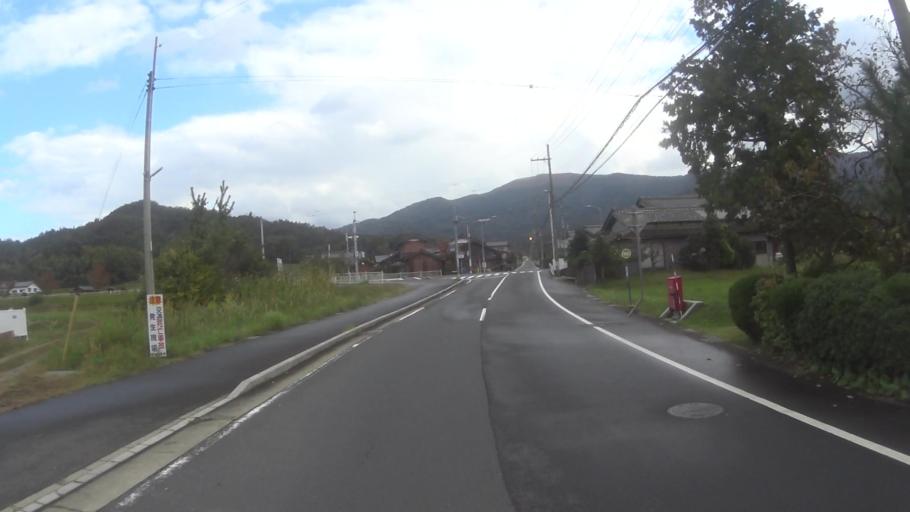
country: JP
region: Kyoto
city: Miyazu
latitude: 35.5014
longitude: 135.1023
